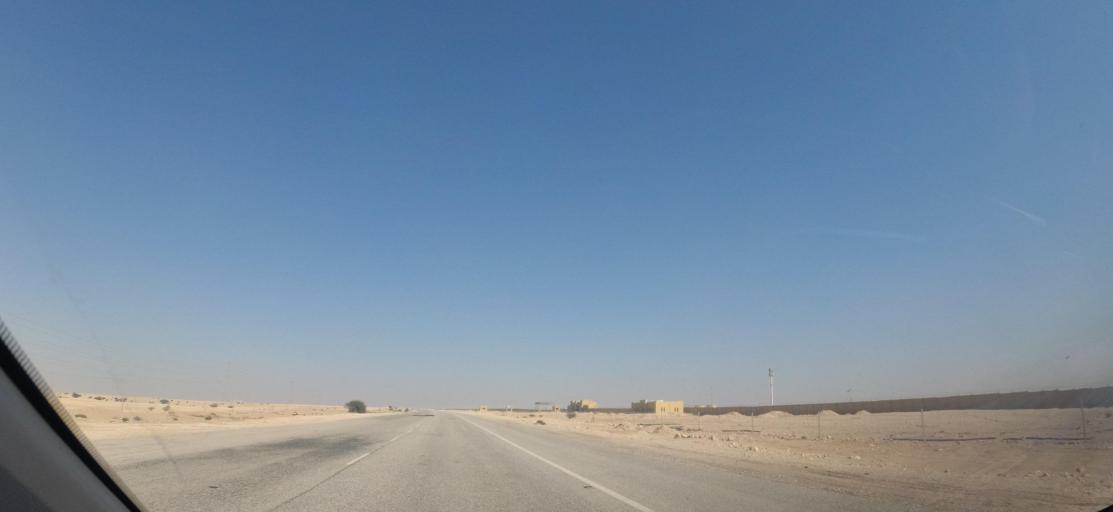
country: QA
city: Al Jumayliyah
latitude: 25.4849
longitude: 50.9701
